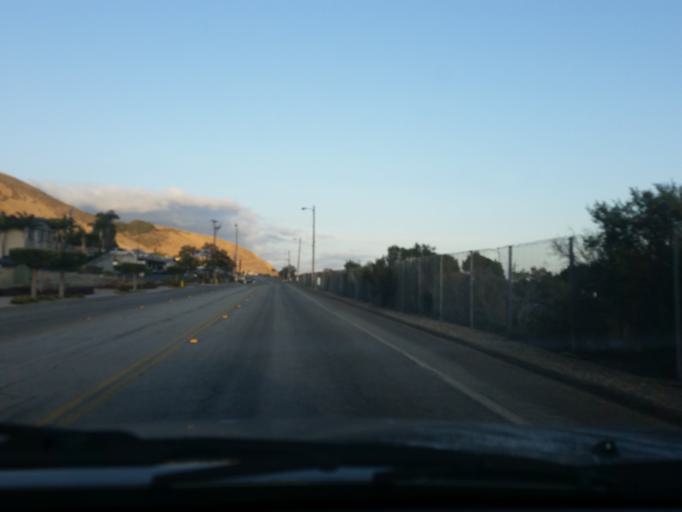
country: US
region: California
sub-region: San Luis Obispo County
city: Pismo Beach
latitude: 35.1577
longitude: -120.6706
